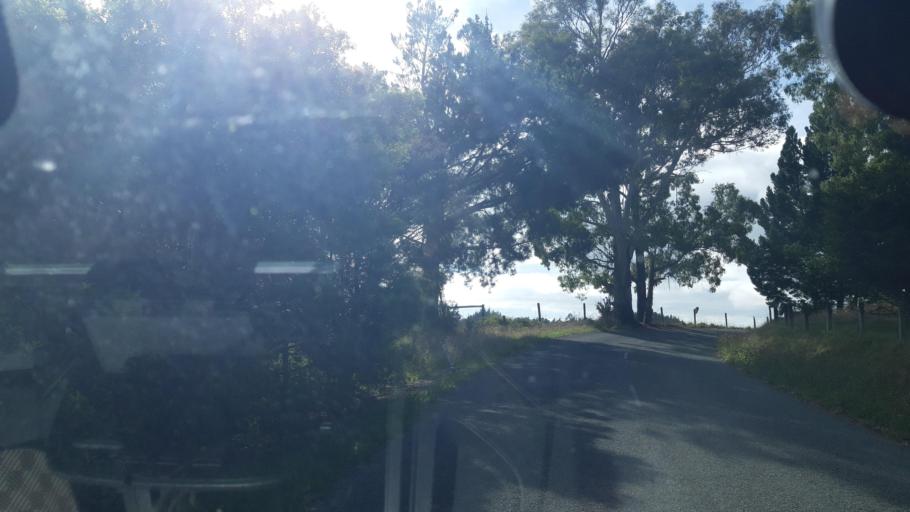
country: NZ
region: Tasman
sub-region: Tasman District
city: Mapua
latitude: -41.2545
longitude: 173.0241
